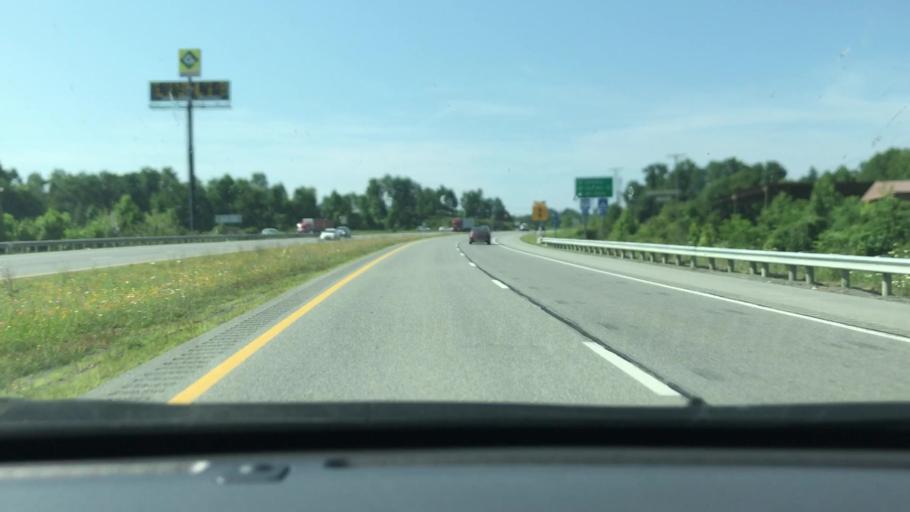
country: US
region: West Virginia
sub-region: Nicholas County
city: Summersville
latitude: 38.2130
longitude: -80.8521
